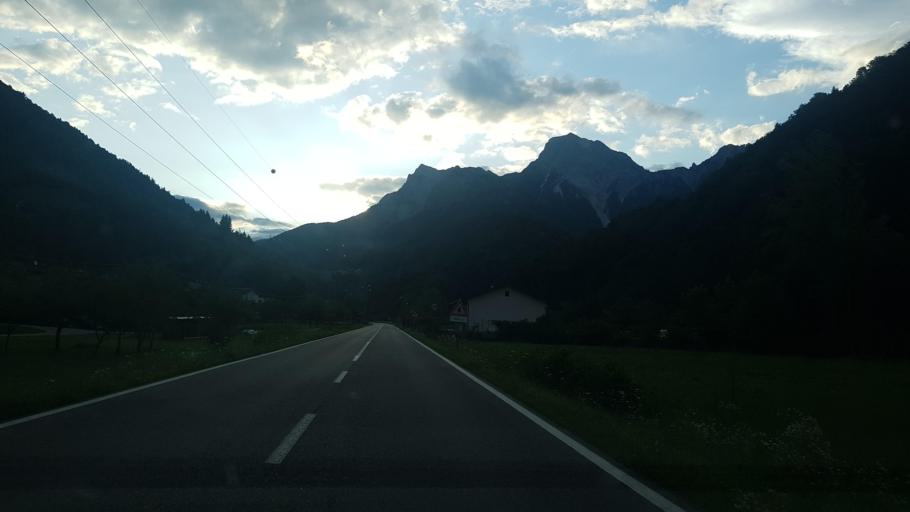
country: IT
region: Friuli Venezia Giulia
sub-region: Provincia di Udine
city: Zuglio
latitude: 46.4686
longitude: 13.0613
